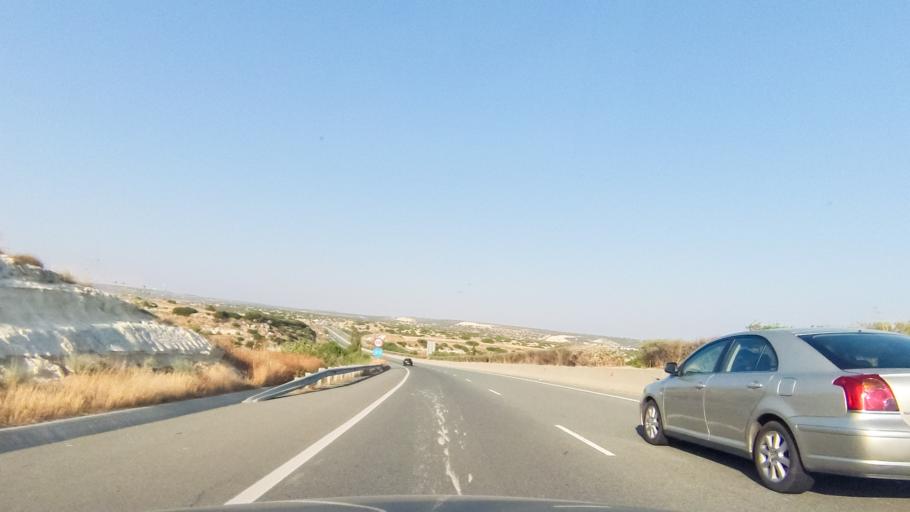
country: CY
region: Limassol
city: Pissouri
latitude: 34.6823
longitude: 32.7661
